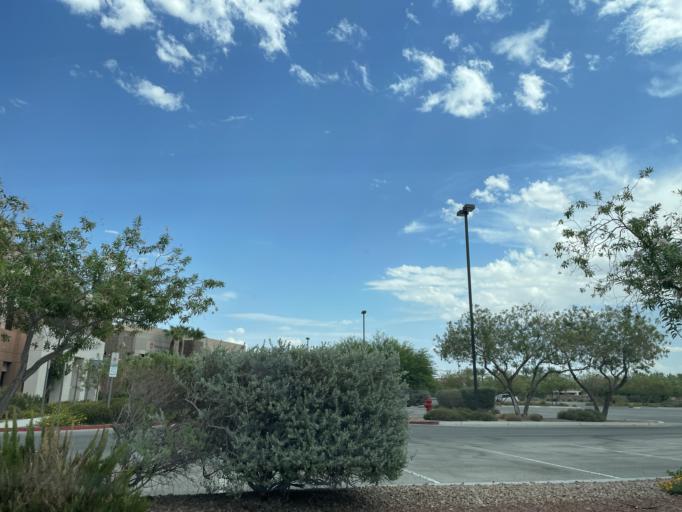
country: US
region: Nevada
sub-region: Clark County
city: North Las Vegas
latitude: 36.2889
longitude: -115.1779
